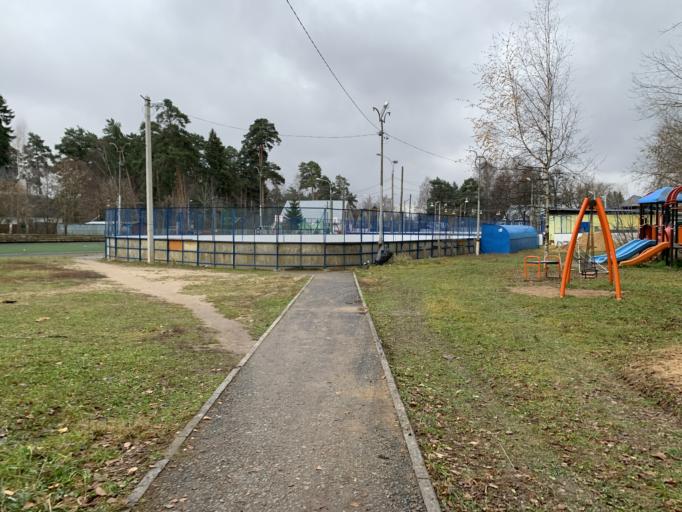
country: RU
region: Moskovskaya
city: Mamontovka
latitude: 55.9845
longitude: 37.8137
